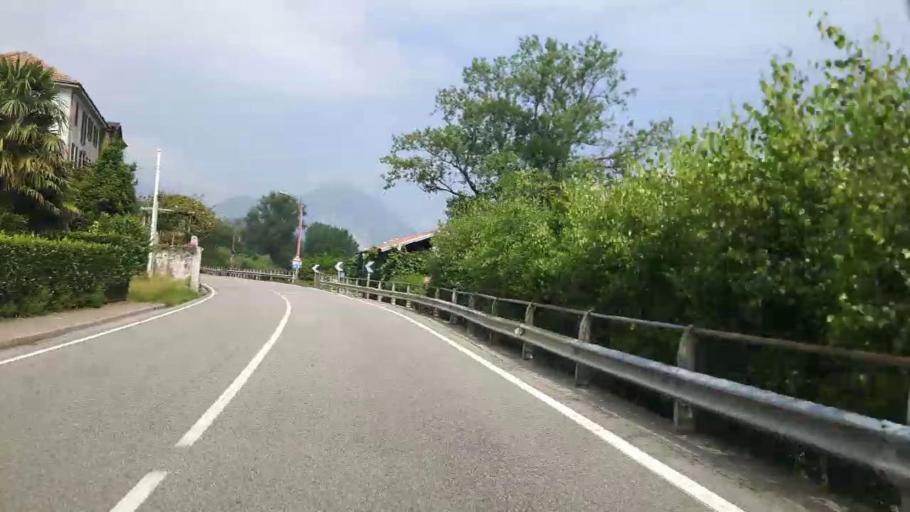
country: IT
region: Piedmont
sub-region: Provincia Verbano-Cusio-Ossola
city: Baveno
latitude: 45.9161
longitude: 8.5013
